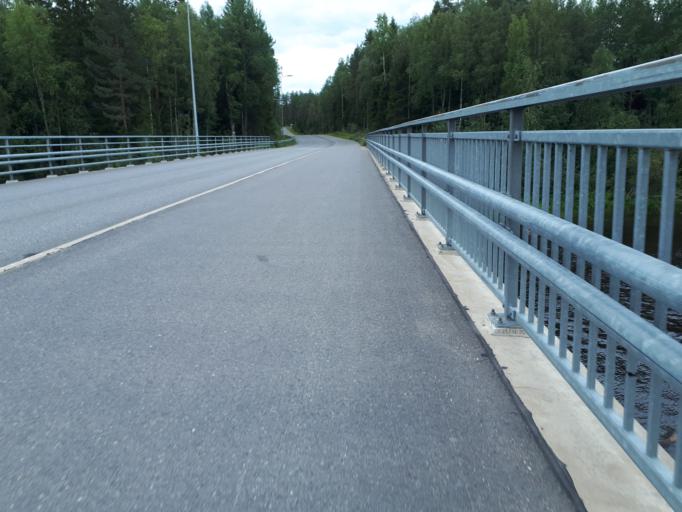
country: FI
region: Northern Ostrobothnia
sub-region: Oulunkaari
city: Ii
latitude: 65.3223
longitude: 25.4100
